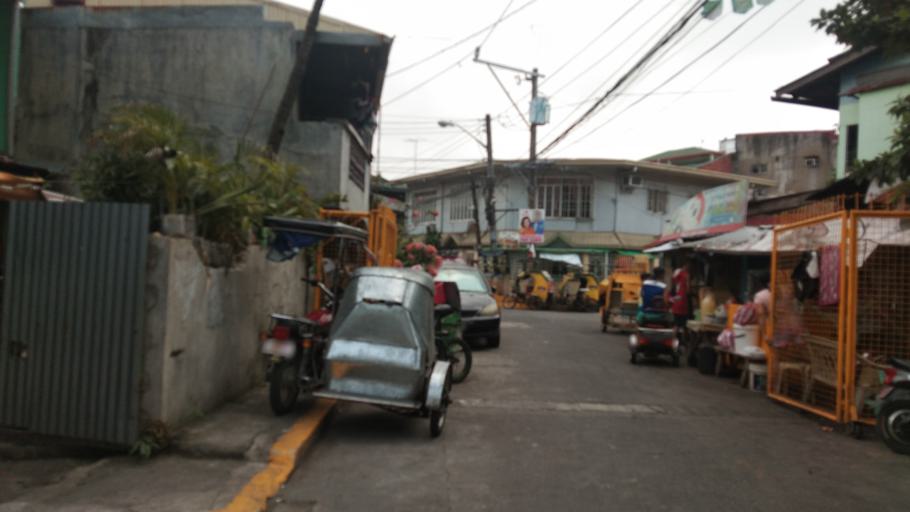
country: PH
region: Metro Manila
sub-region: City of Manila
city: Quiapo
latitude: 14.5762
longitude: 120.9982
